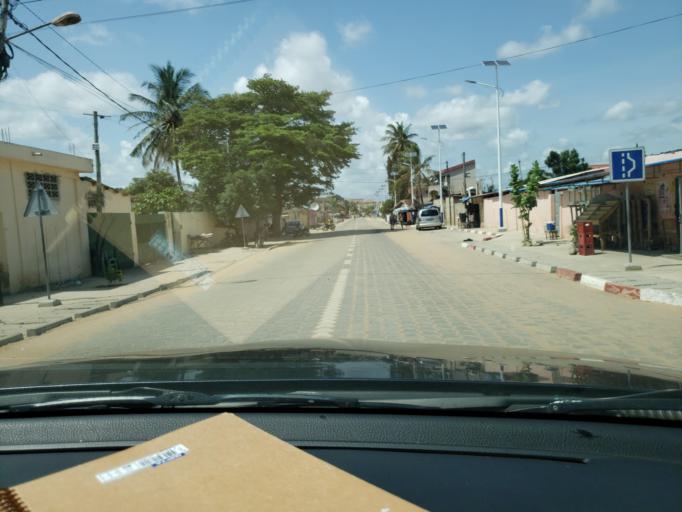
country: TG
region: Maritime
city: Lome
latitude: 6.1888
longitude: 1.1977
